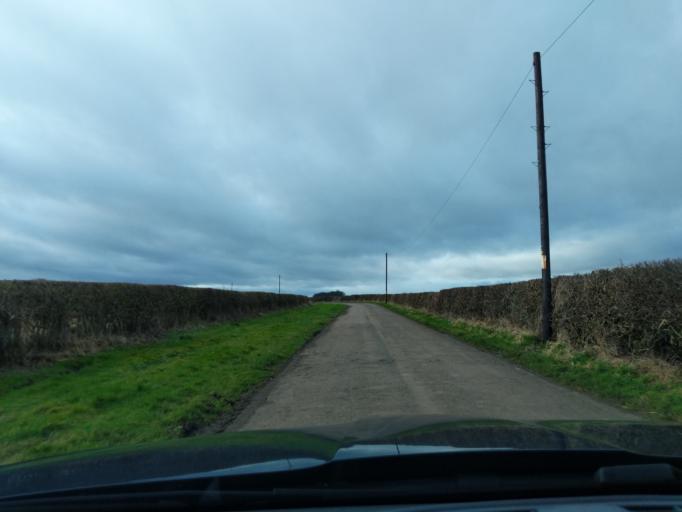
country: GB
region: England
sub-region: Northumberland
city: Ancroft
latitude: 55.6958
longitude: -1.9802
